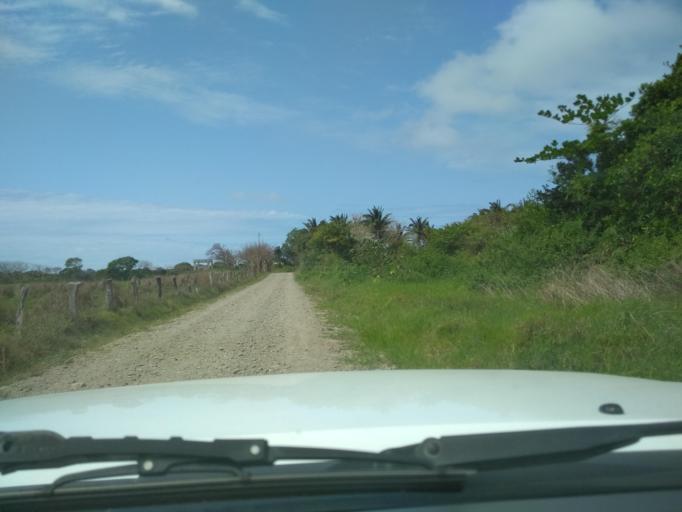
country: MX
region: Veracruz
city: Anton Lizardo
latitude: 19.0268
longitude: -95.9687
